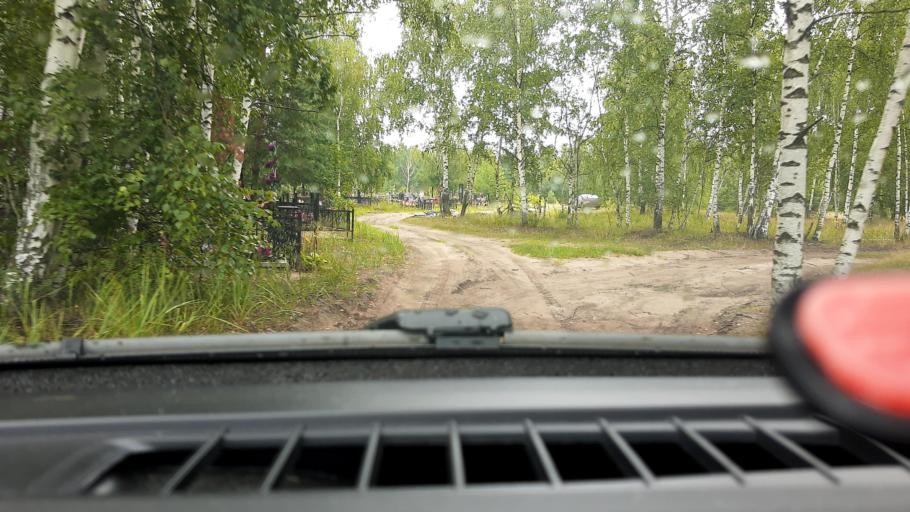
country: RU
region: Nizjnij Novgorod
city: Gorbatovka
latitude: 56.3531
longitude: 43.7822
